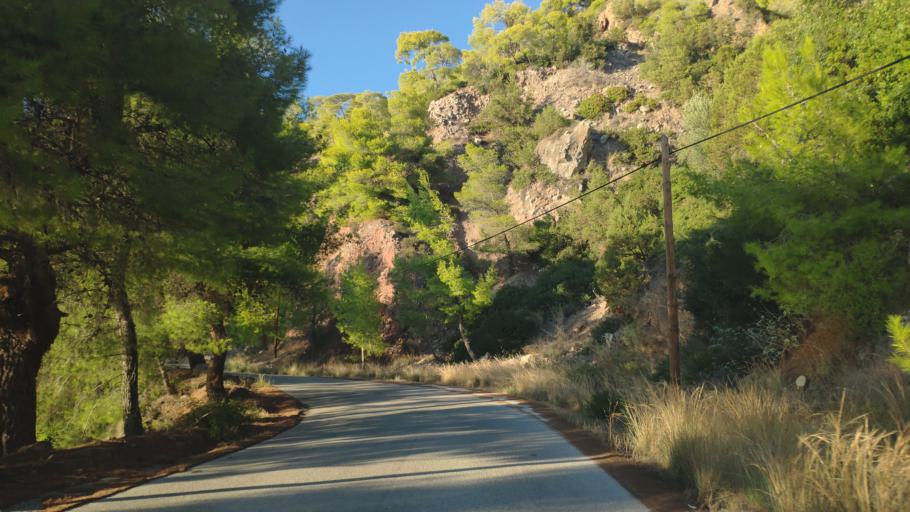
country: GR
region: Attica
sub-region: Nomos Piraios
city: Megalochori
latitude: 37.6067
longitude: 23.3307
